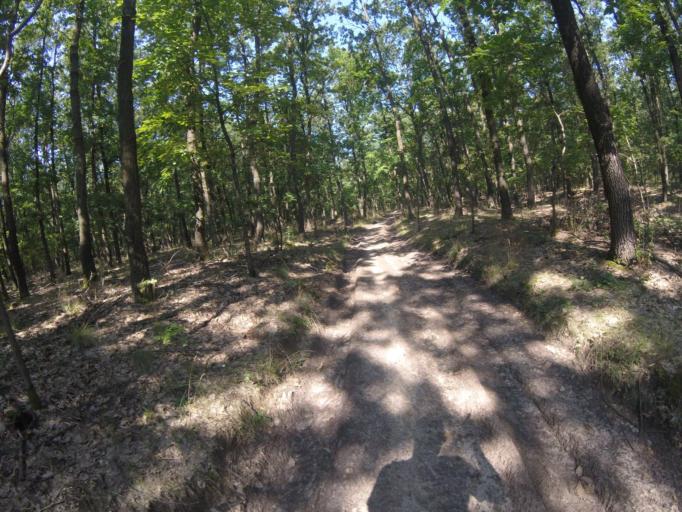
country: HU
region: Nograd
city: Bujak
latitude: 47.8887
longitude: 19.5279
